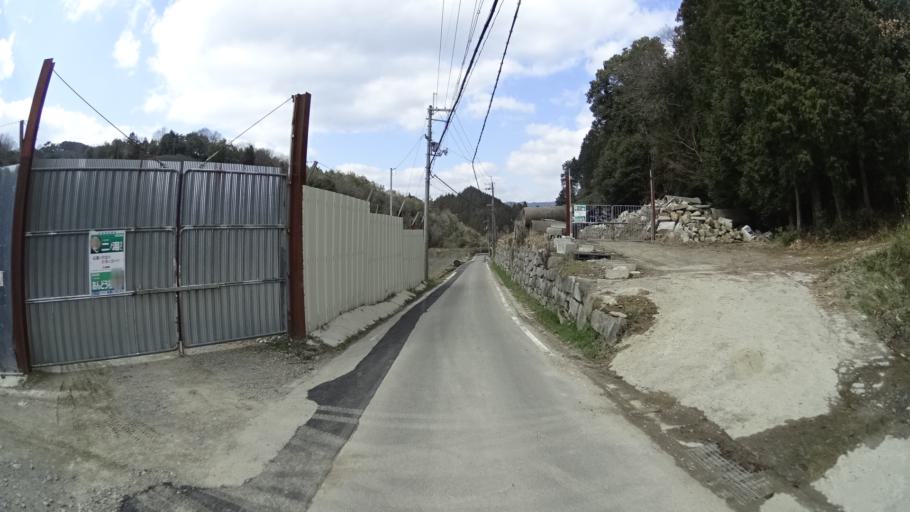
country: JP
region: Nara
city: Nara-shi
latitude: 34.7775
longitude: 135.9079
